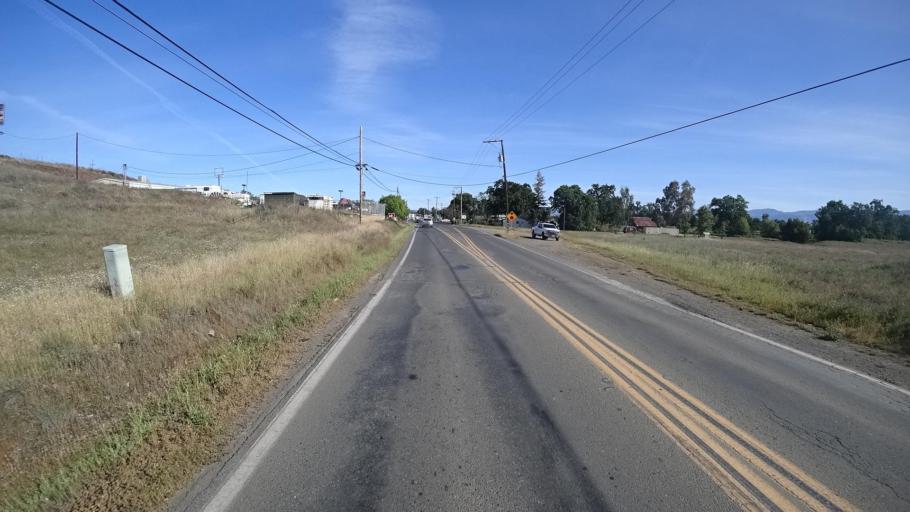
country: US
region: California
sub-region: Lake County
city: Lakeport
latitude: 39.0157
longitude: -122.9109
